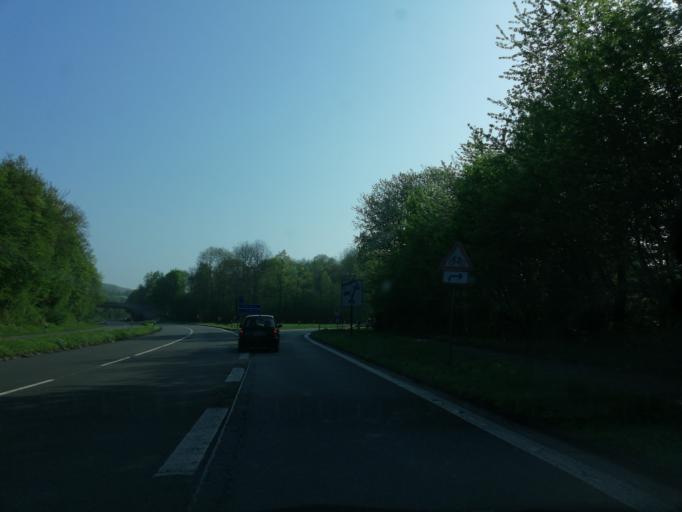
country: DE
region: North Rhine-Westphalia
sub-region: Regierungsbezirk Arnsberg
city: Schwelm
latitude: 51.2839
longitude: 7.2604
